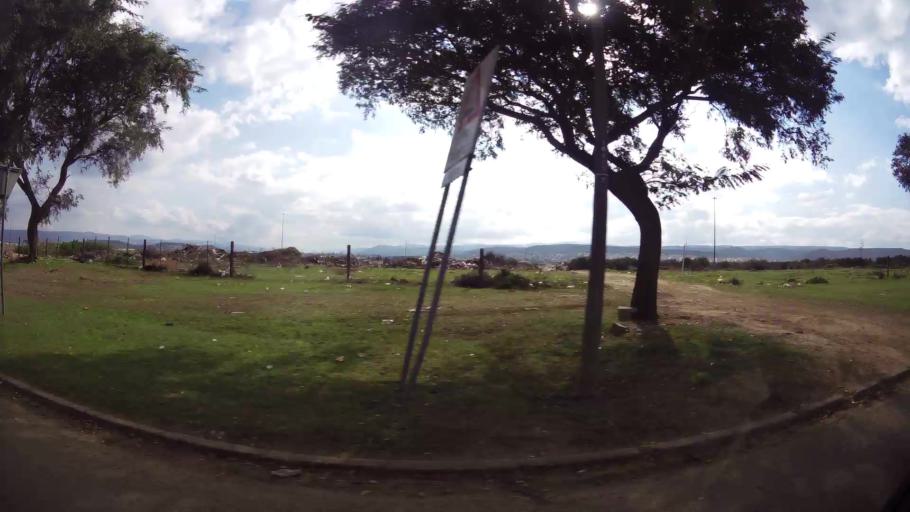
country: ZA
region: Eastern Cape
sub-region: Nelson Mandela Bay Metropolitan Municipality
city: Uitenhage
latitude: -33.7464
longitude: 25.4011
